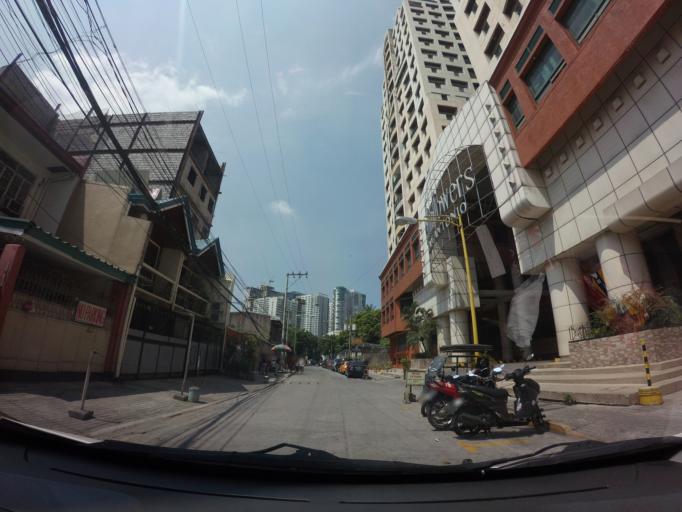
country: PH
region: Metro Manila
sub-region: Makati City
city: Makati City
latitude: 14.5636
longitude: 121.0105
